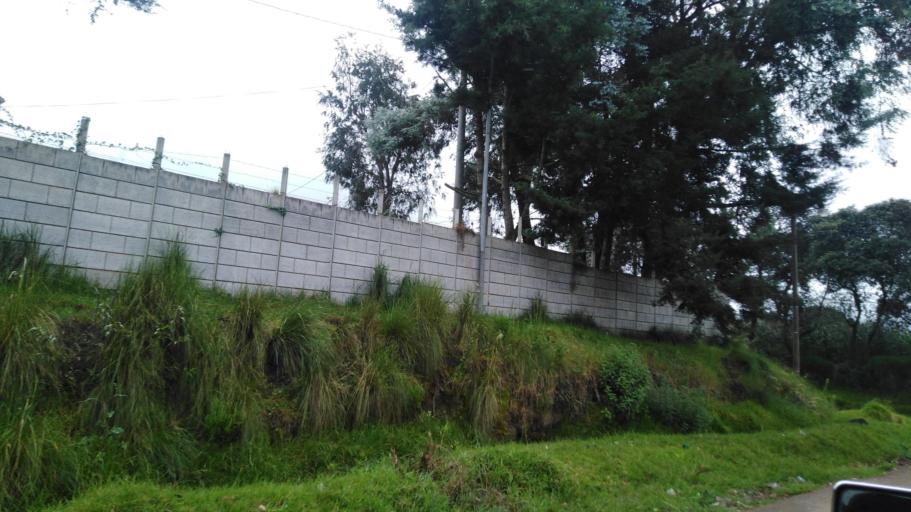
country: GT
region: Quetzaltenango
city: Quetzaltenango
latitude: 14.8552
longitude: -91.5043
